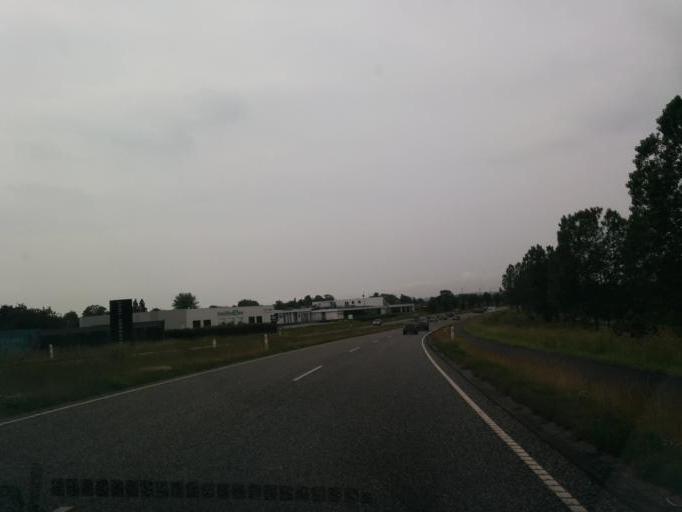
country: DK
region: Central Jutland
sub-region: Arhus Kommune
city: Hjortshoj
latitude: 56.2106
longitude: 10.2764
